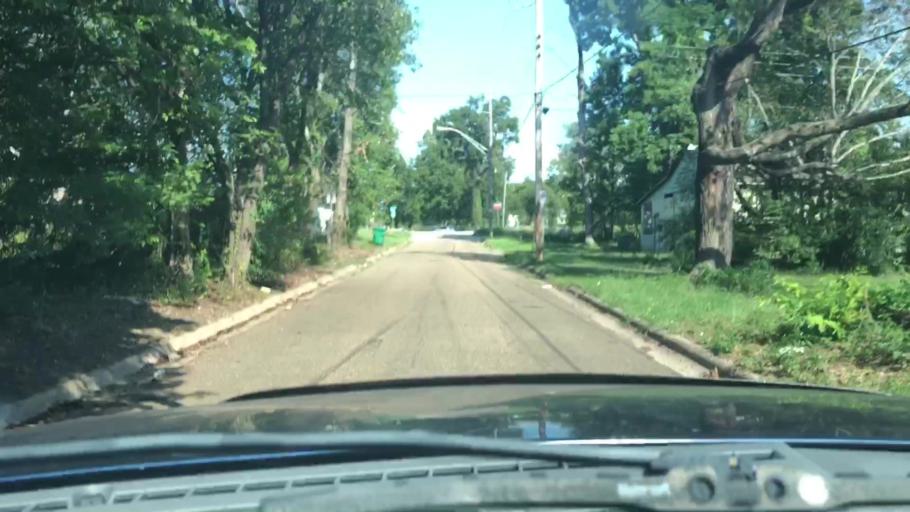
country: US
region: Texas
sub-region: Bowie County
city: Texarkana
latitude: 33.4167
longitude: -94.0621
